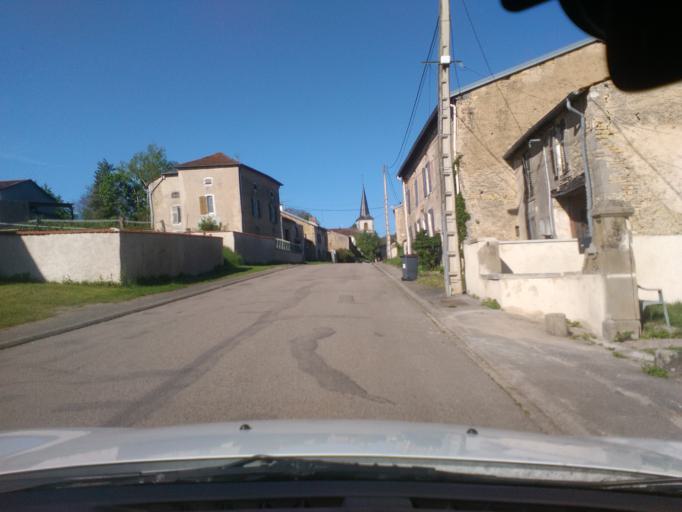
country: FR
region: Lorraine
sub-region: Departement des Vosges
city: Charmes
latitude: 48.3349
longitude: 6.2363
